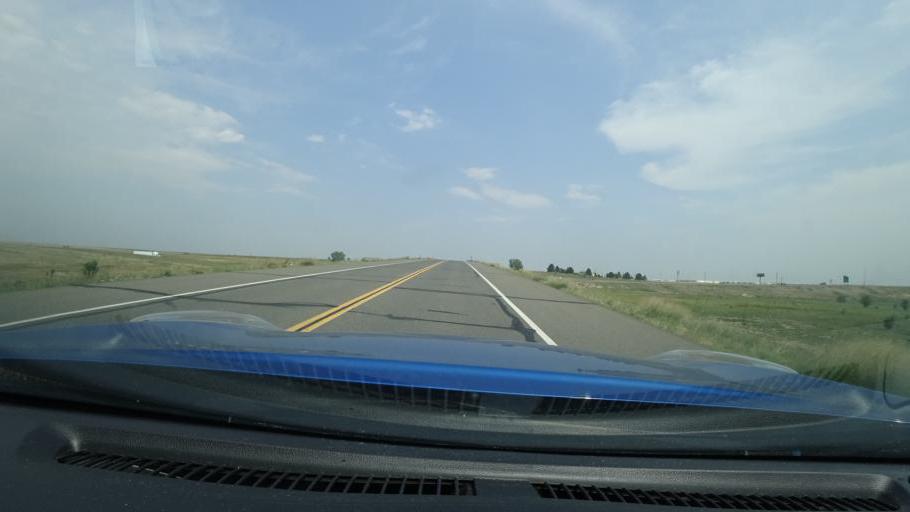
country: US
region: Colorado
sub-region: Adams County
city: Aurora
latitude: 39.7547
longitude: -104.7193
